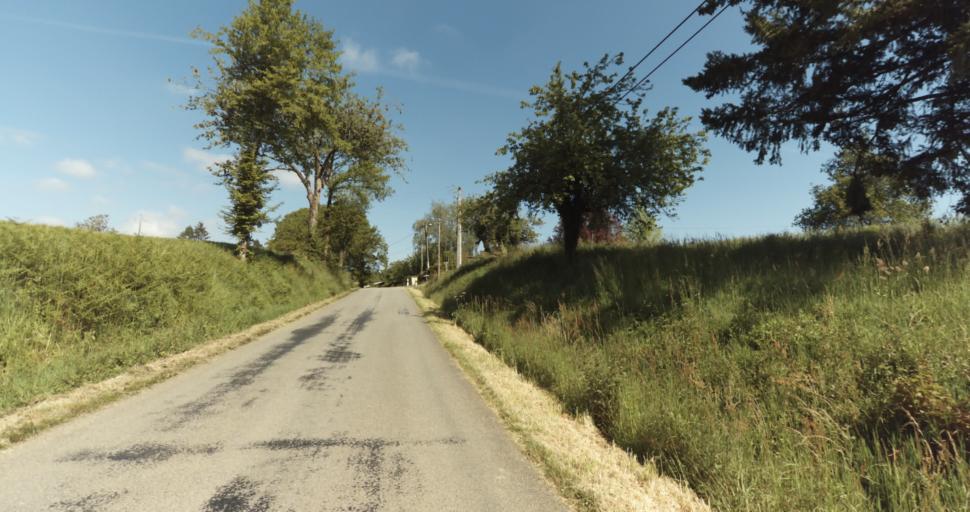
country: FR
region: Limousin
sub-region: Departement de la Haute-Vienne
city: Le Vigen
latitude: 45.7113
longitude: 1.2960
